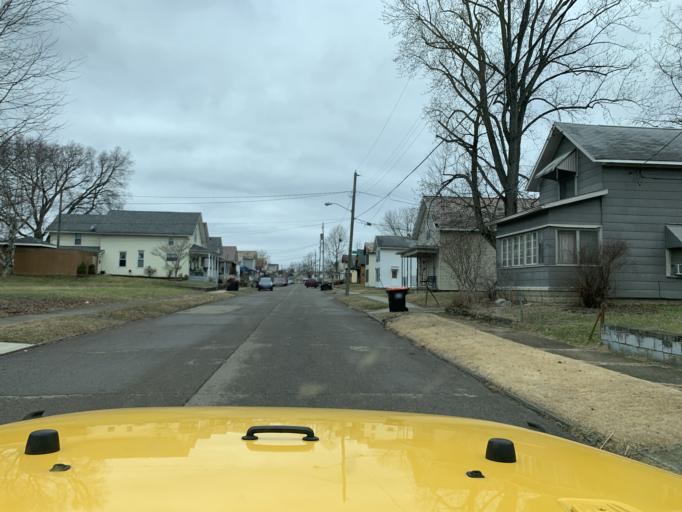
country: US
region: Ohio
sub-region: Licking County
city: Newark
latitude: 40.0503
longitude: -82.4045
